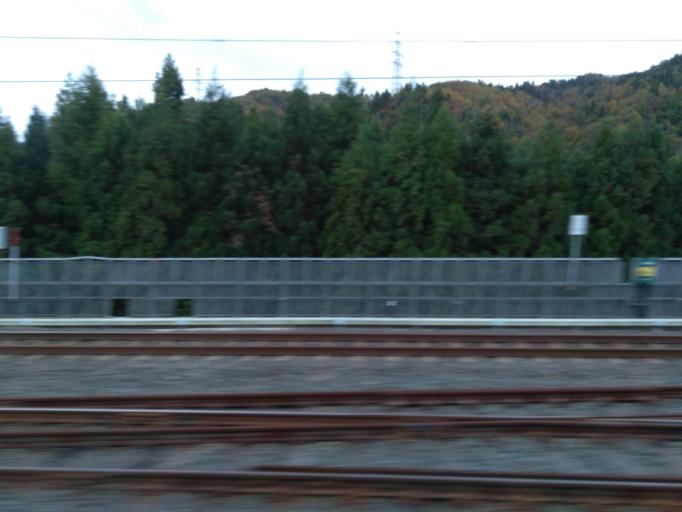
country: JP
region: Aomori
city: Goshogawara
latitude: 41.1492
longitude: 140.5118
